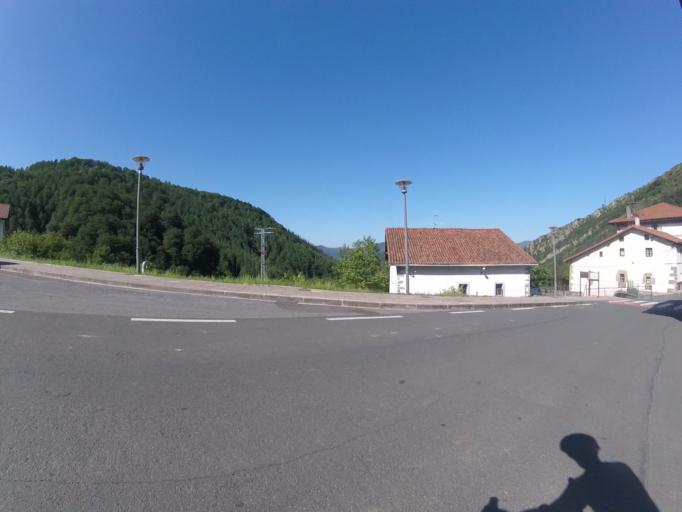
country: ES
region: Basque Country
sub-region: Provincia de Guipuzcoa
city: Beizama
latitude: 43.1339
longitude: -2.1994
